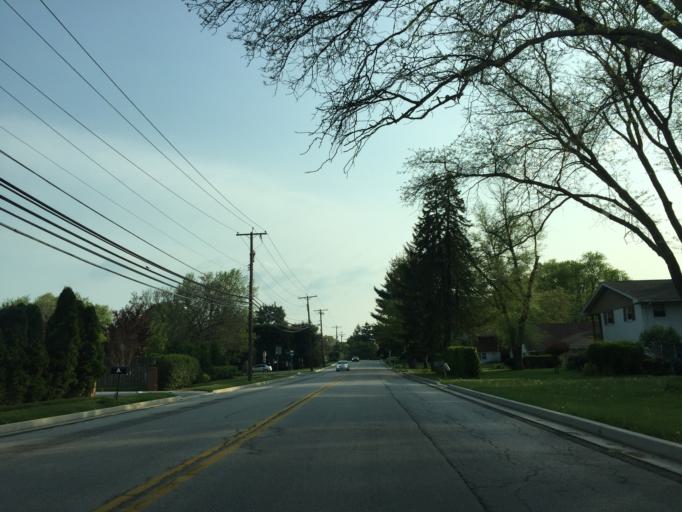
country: US
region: Maryland
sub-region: Baltimore County
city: Pikesville
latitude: 39.3830
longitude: -76.7150
